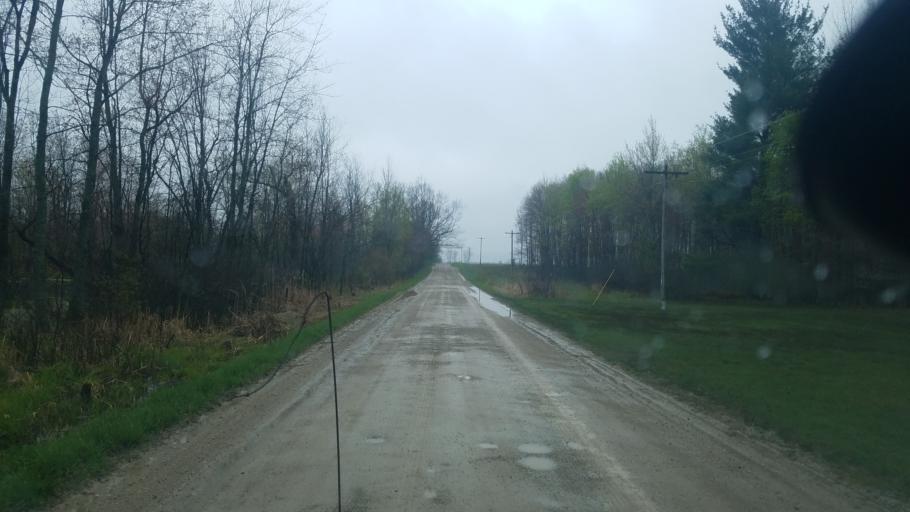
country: US
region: Michigan
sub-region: Montcalm County
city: Lakeview
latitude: 43.4754
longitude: -85.2937
